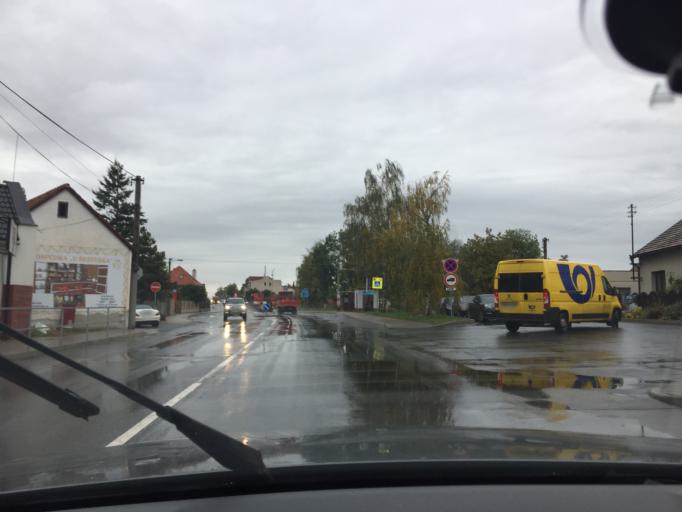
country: CZ
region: Central Bohemia
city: Klecany
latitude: 50.2004
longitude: 14.4352
